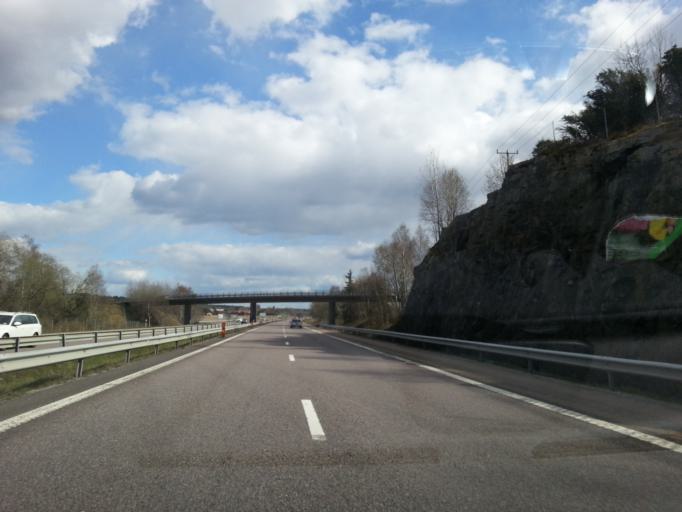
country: SE
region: Vaestra Goetaland
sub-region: Kungalvs Kommun
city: Kode
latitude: 57.9044
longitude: 11.9097
